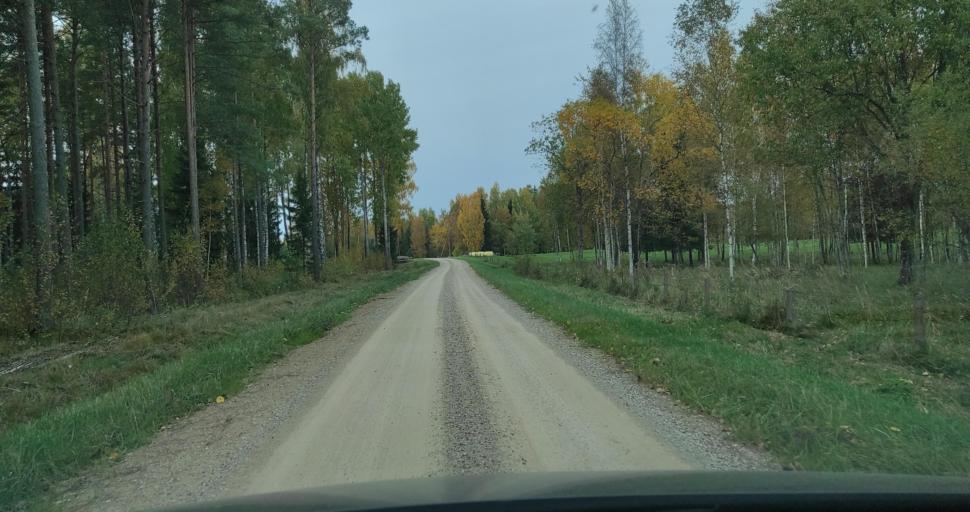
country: LV
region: Kuldigas Rajons
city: Kuldiga
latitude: 57.0250
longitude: 22.1995
